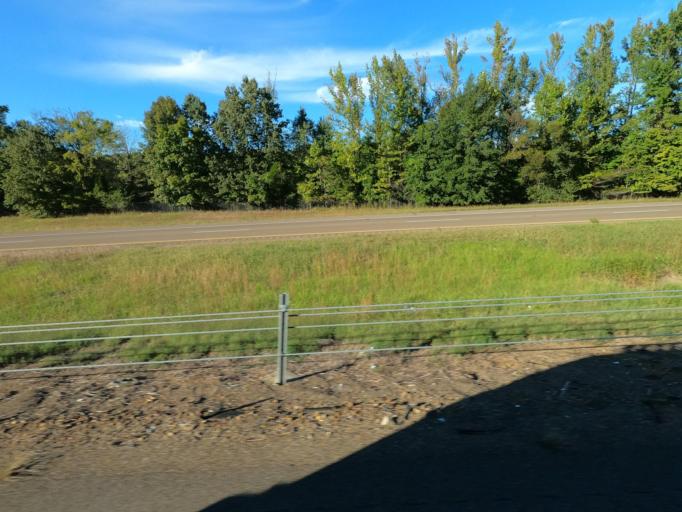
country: US
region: Tennessee
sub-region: Shelby County
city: Germantown
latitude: 35.0269
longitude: -89.7517
